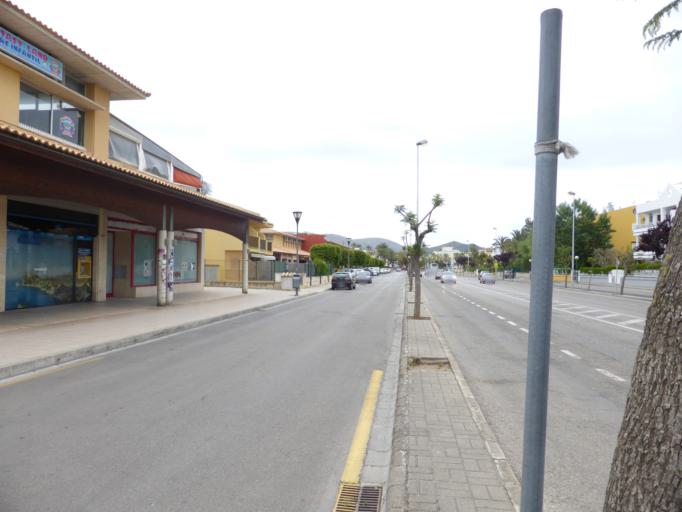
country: ES
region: Balearic Islands
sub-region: Illes Balears
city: Port d'Alcudia
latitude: 39.8403
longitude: 3.1228
